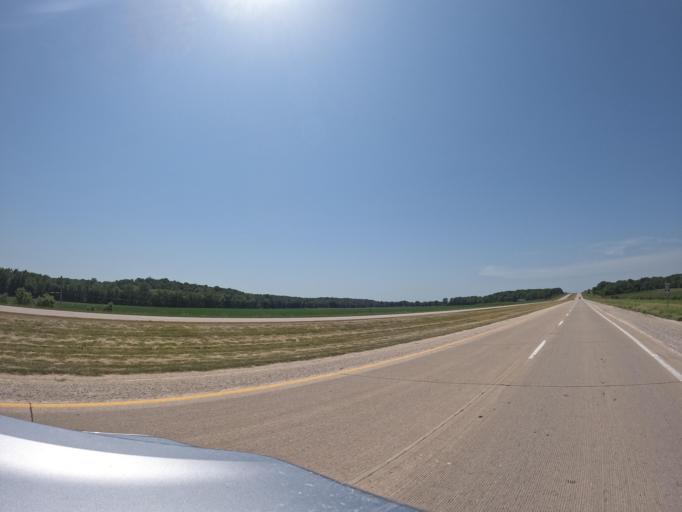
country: US
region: Iowa
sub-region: Henry County
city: Mount Pleasant
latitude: 40.9712
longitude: -91.6443
